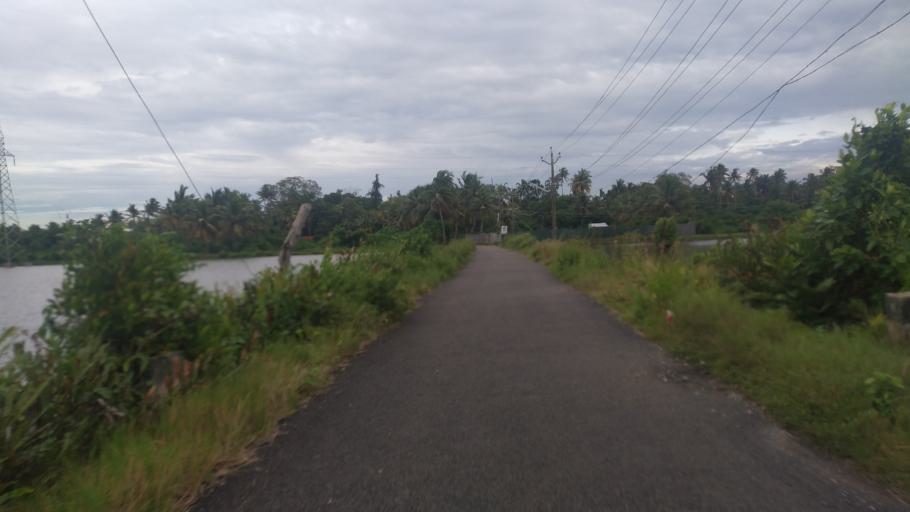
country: IN
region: Kerala
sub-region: Alappuzha
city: Arukutti
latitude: 9.8710
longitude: 76.2828
